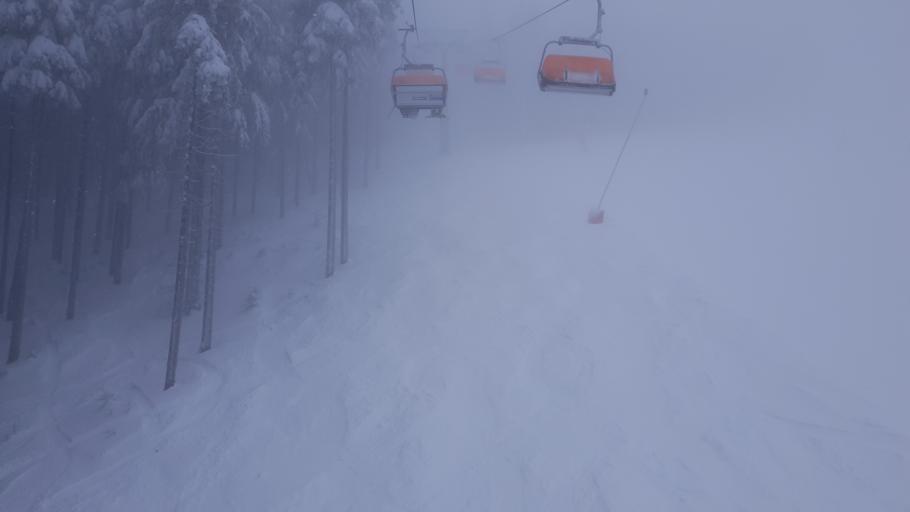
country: DE
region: Saxony
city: Kurort Oberwiesenthal
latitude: 50.3896
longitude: 12.9547
